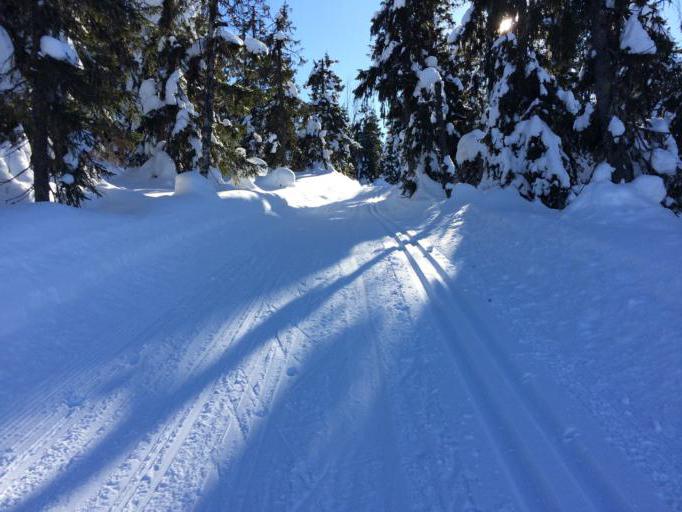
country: NO
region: Oppland
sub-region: Gausdal
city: Segalstad bru
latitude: 61.3117
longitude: 10.1040
